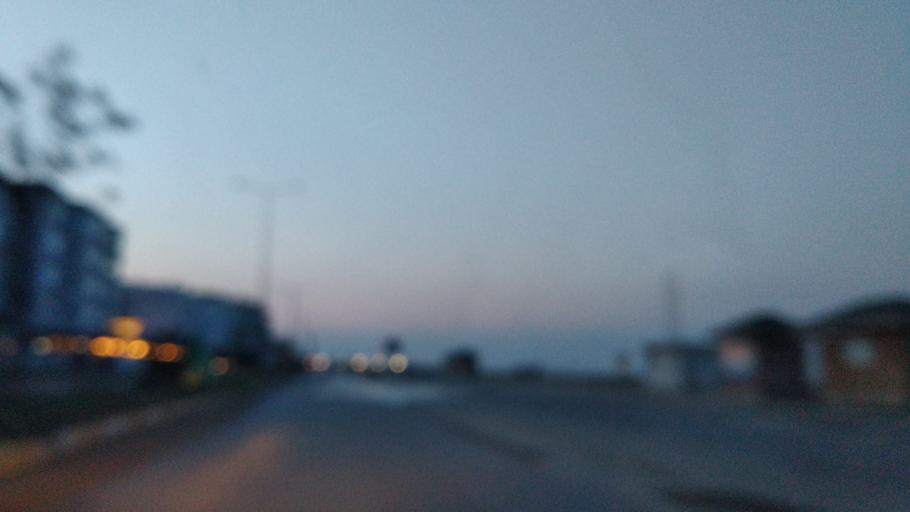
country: TR
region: Sakarya
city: Karasu
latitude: 41.1009
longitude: 30.7181
